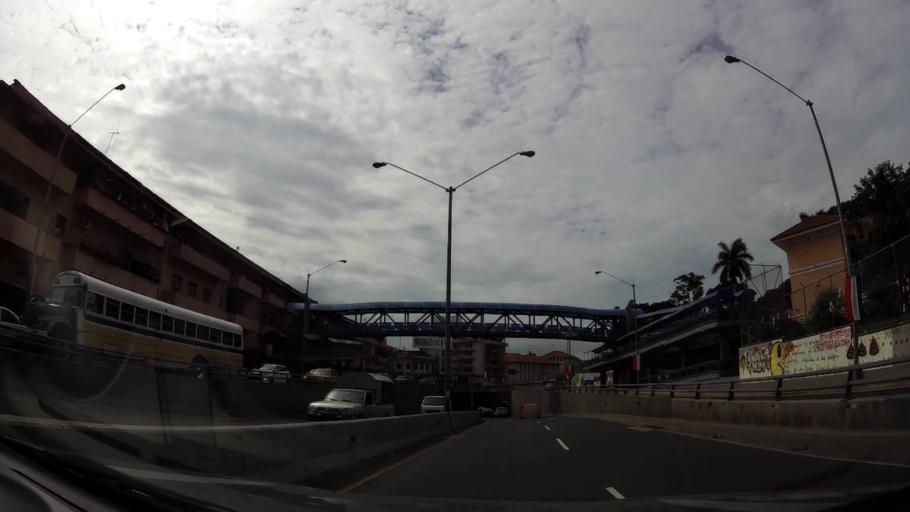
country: PA
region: Panama
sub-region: Distrito de Panama
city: Ancon
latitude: 8.9604
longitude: -79.5428
